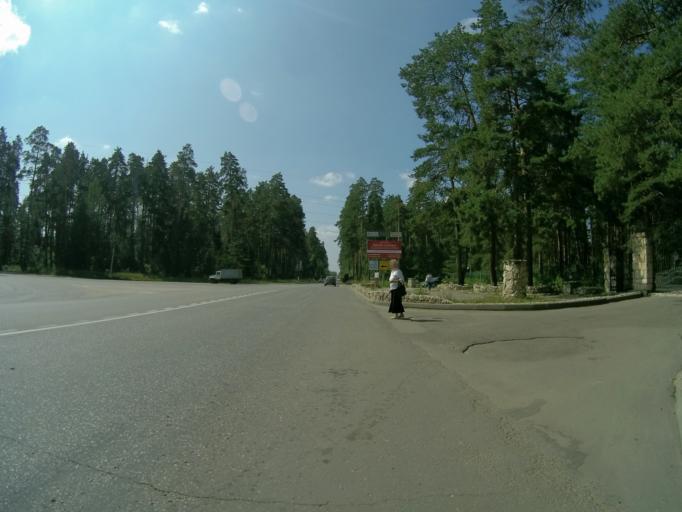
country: RU
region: Vladimir
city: Gus'-Khrustal'nyy
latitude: 55.6330
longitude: 40.6945
